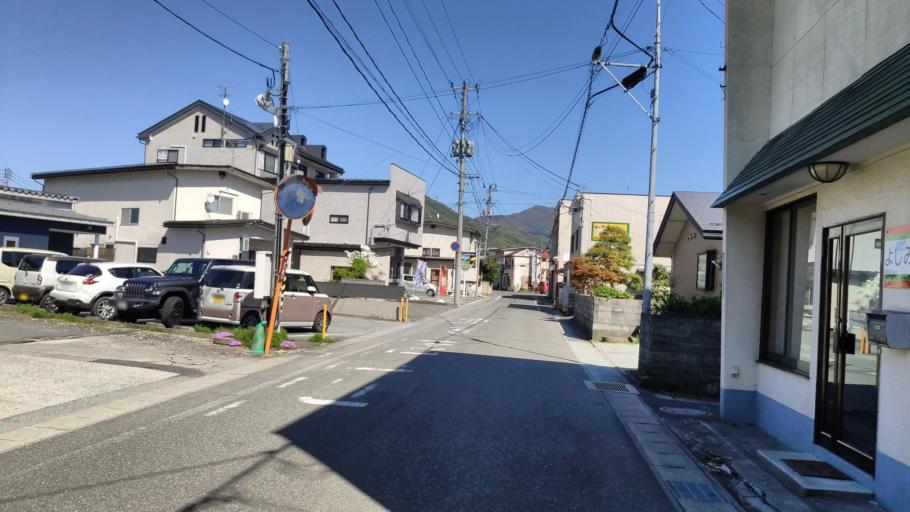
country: JP
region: Yamagata
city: Tendo
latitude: 38.3595
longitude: 140.3737
